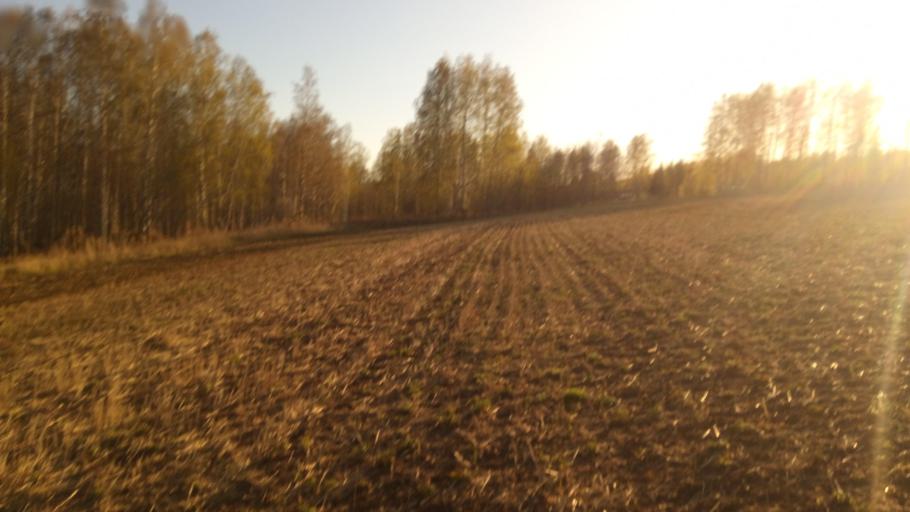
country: RU
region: Chelyabinsk
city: Timiryazevskiy
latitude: 54.9943
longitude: 60.8630
